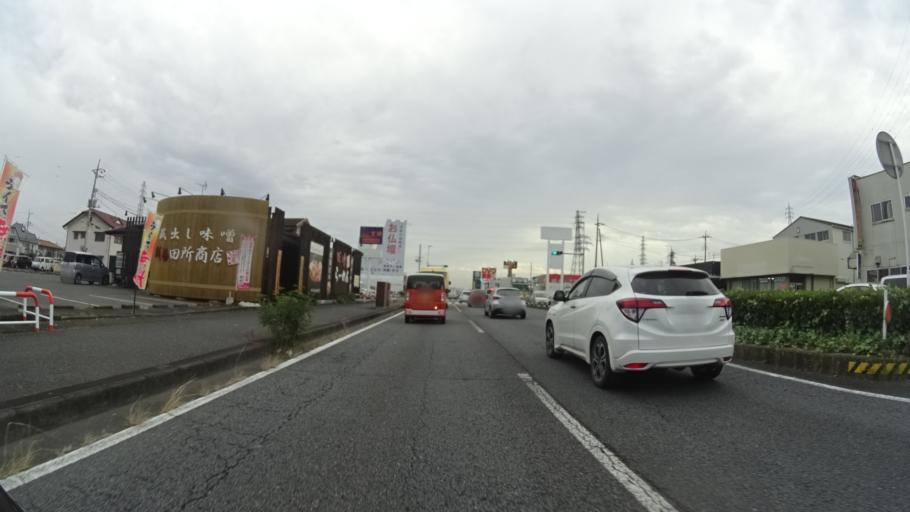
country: JP
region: Gunma
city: Maebashi-shi
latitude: 36.3815
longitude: 139.1023
